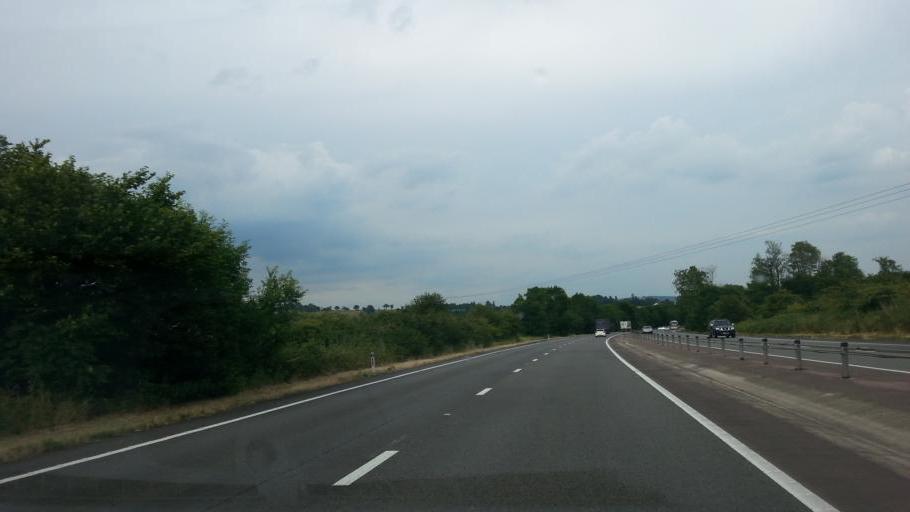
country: GB
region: Wales
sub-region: Monmouthshire
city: Mitchel Troy
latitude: 51.7877
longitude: -2.7712
